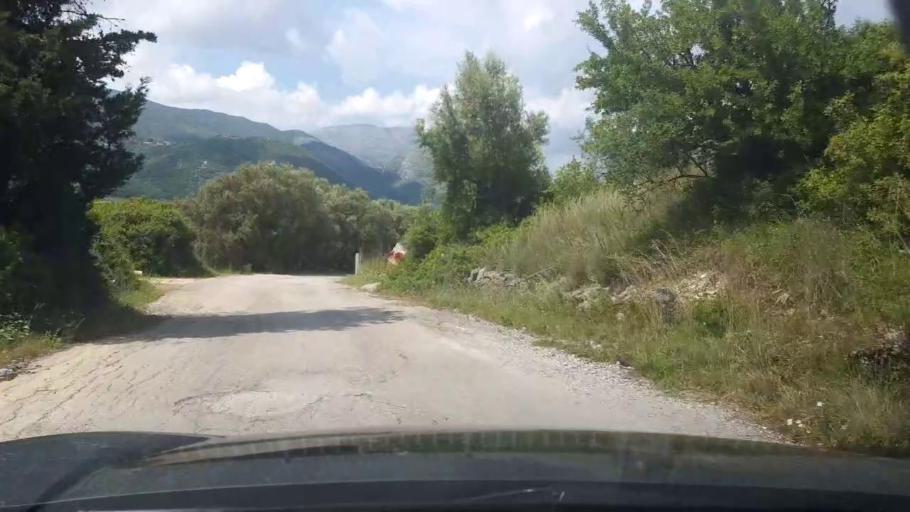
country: GR
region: Ionian Islands
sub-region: Lefkada
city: Nidri
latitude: 38.6456
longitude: 20.7050
